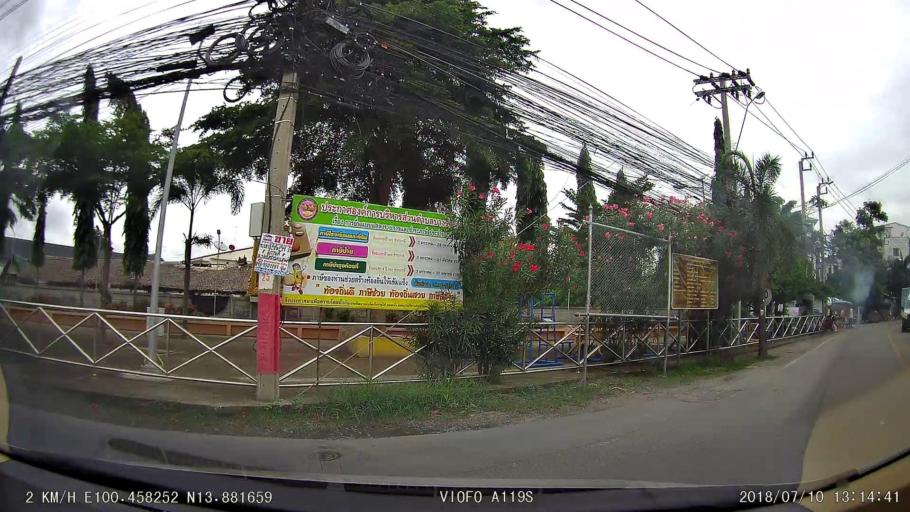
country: TH
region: Nonthaburi
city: Bang Bua Thong
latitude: 13.8816
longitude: 100.4584
